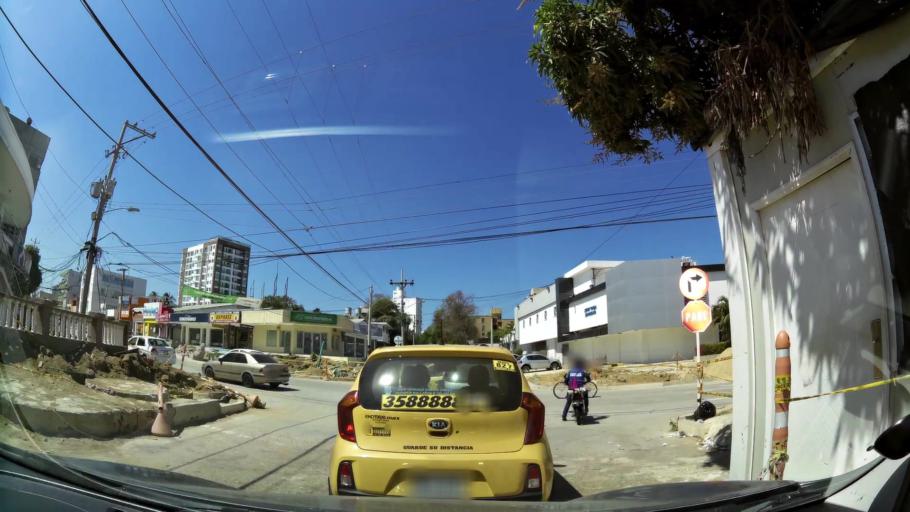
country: CO
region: Atlantico
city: Barranquilla
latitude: 10.9993
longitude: -74.8084
